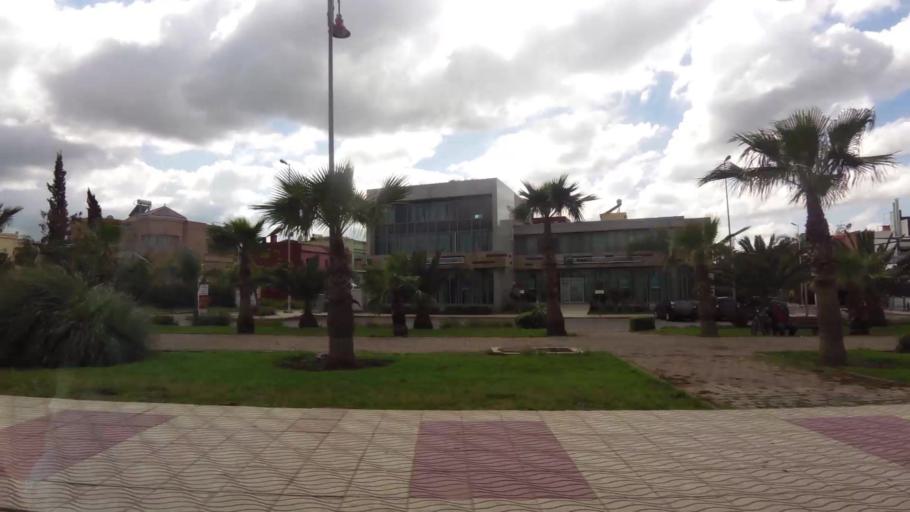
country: MA
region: Chaouia-Ouardigha
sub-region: Settat Province
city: Berrechid
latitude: 33.2798
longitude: -7.5900
